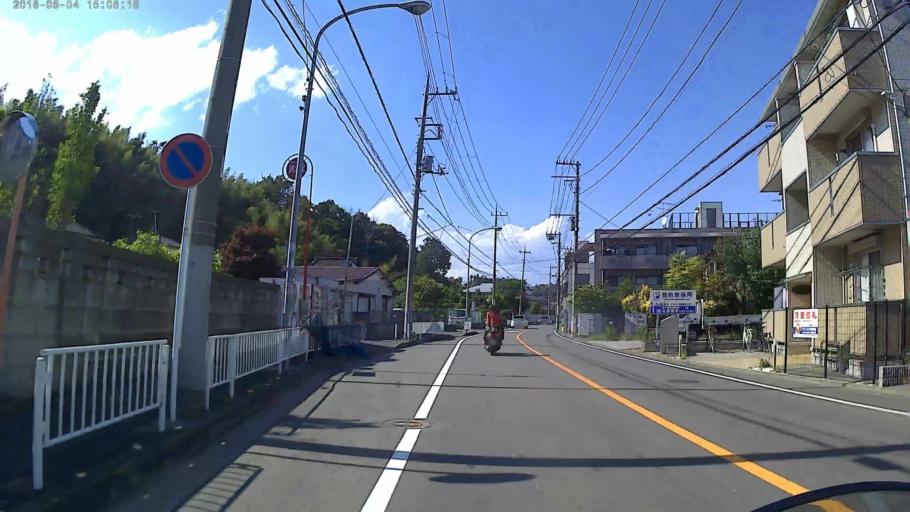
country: JP
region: Kanagawa
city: Yokohama
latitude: 35.5178
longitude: 139.6100
